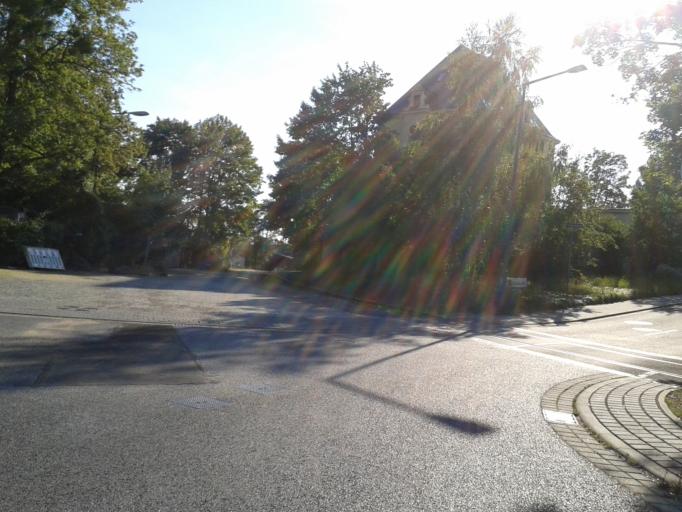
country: DE
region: Saxony
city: Albertstadt
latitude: 51.0808
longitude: 13.7649
